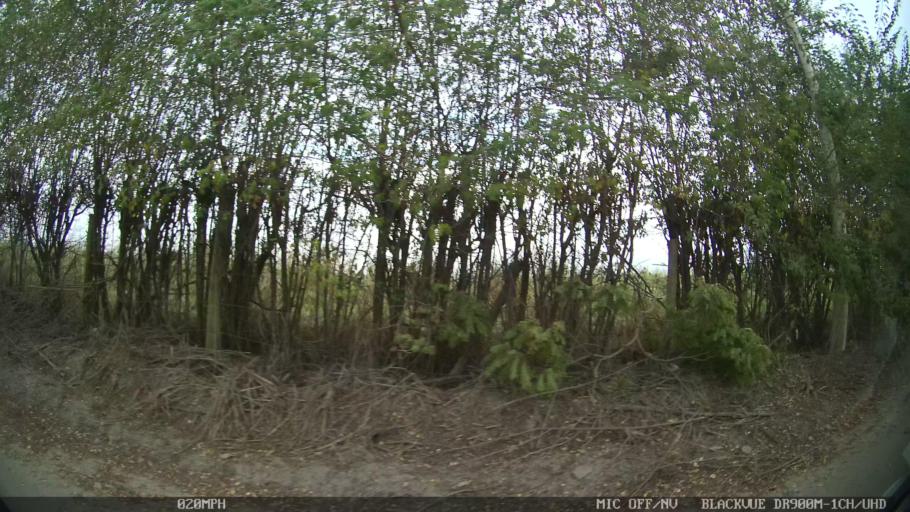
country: BR
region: Sao Paulo
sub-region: Americana
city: Americana
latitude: -22.6720
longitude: -47.3740
